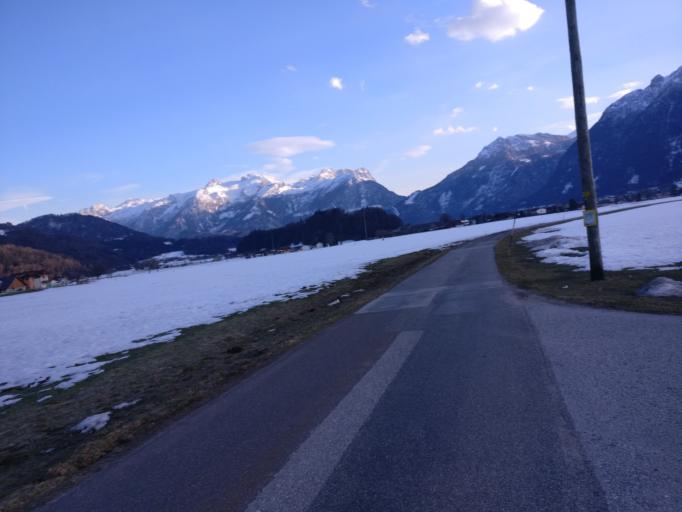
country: AT
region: Salzburg
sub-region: Politischer Bezirk Hallein
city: Kuchl
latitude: 47.6467
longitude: 13.1550
